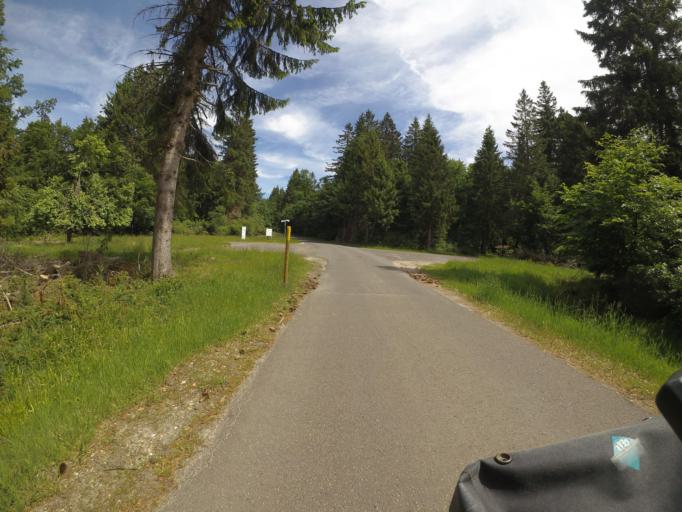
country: DE
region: Rheinland-Pfalz
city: Borfink
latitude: 49.7097
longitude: 7.0699
